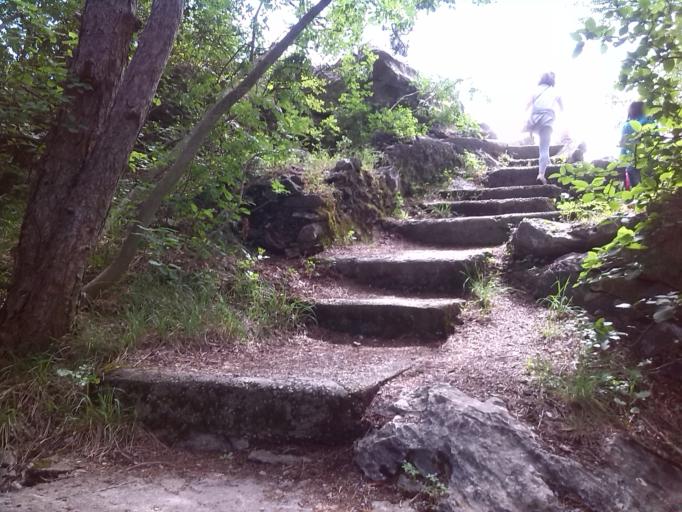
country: IT
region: Friuli Venezia Giulia
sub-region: Provincia di Trieste
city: Duino
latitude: 45.7728
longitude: 13.6120
